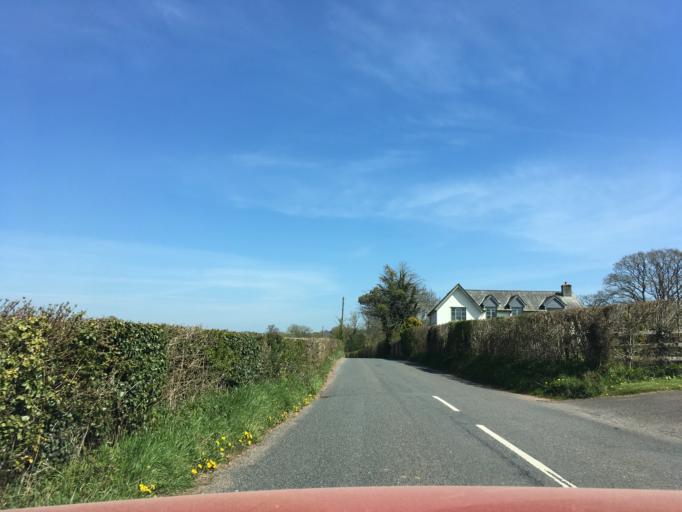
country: GB
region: Wales
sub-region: Monmouthshire
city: Llangwm
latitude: 51.7145
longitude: -2.8478
